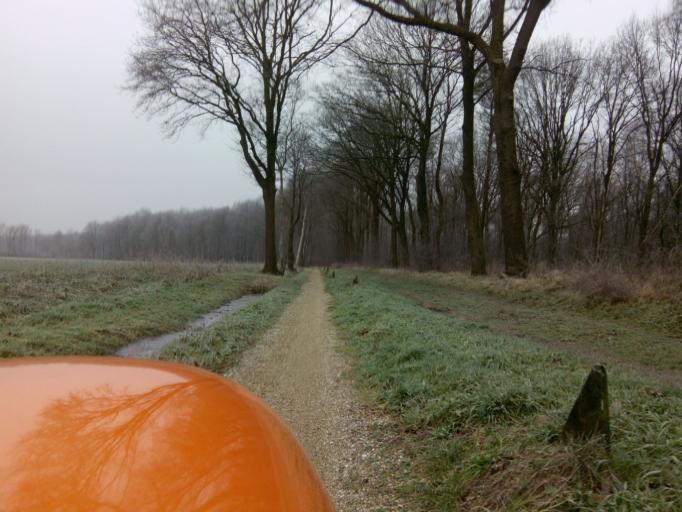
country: NL
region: Gelderland
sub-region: Gemeente Barneveld
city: Voorthuizen
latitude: 52.1902
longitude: 5.5653
